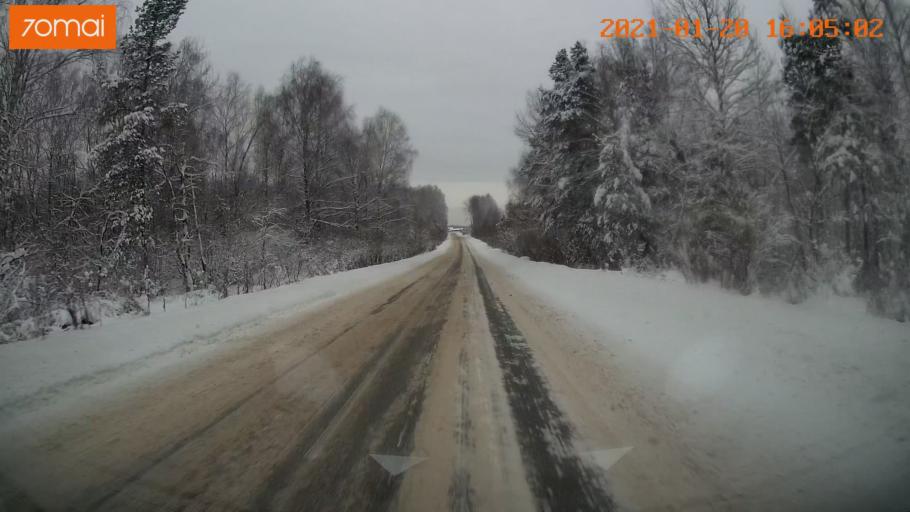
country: RU
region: Vladimir
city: Sudogda
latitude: 56.0620
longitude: 40.8111
